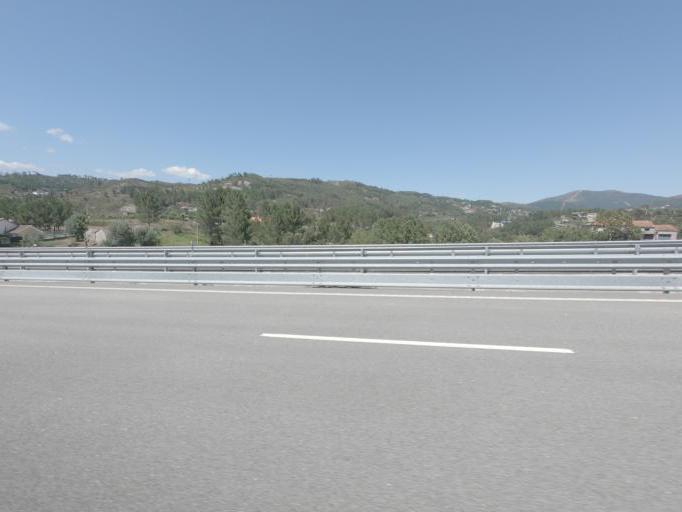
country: PT
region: Porto
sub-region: Amarante
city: Amarante
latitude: 41.2605
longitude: -8.0201
